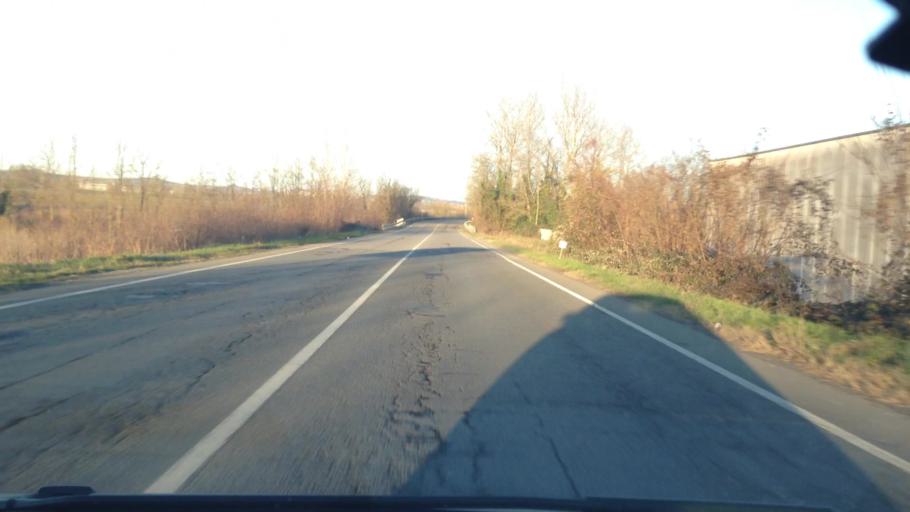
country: IT
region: Piedmont
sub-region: Provincia di Alessandria
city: Solero
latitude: 44.9196
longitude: 8.4992
